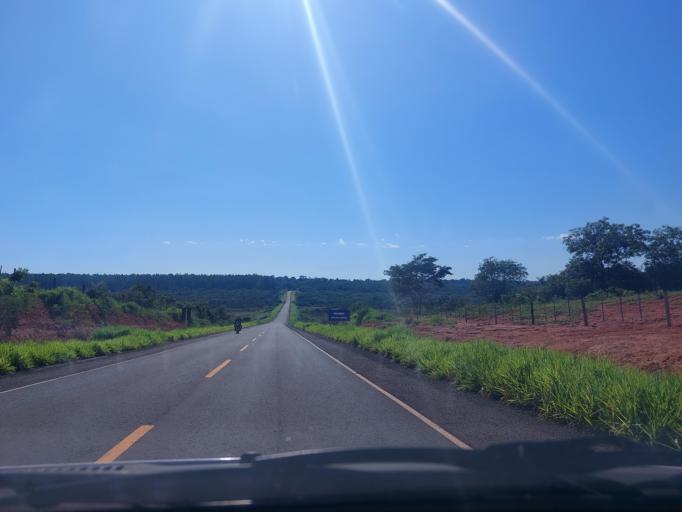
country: PY
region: San Pedro
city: Guayaybi
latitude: -24.2987
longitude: -56.1424
